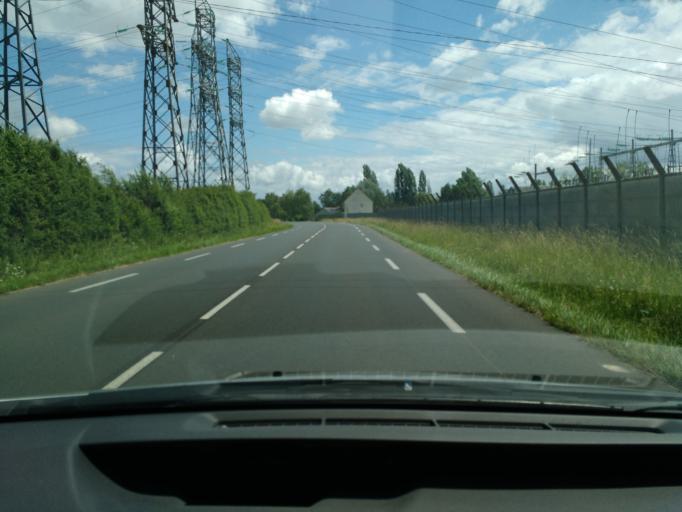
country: FR
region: Pays de la Loire
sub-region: Departement de Maine-et-Loire
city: Trelaze
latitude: 47.4868
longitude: -0.4787
